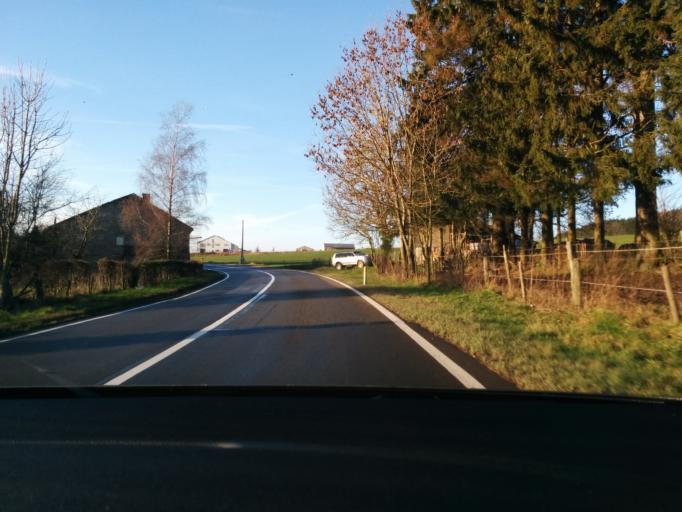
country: BE
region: Wallonia
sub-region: Province de Liege
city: Lierneux
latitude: 50.2625
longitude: 5.8286
